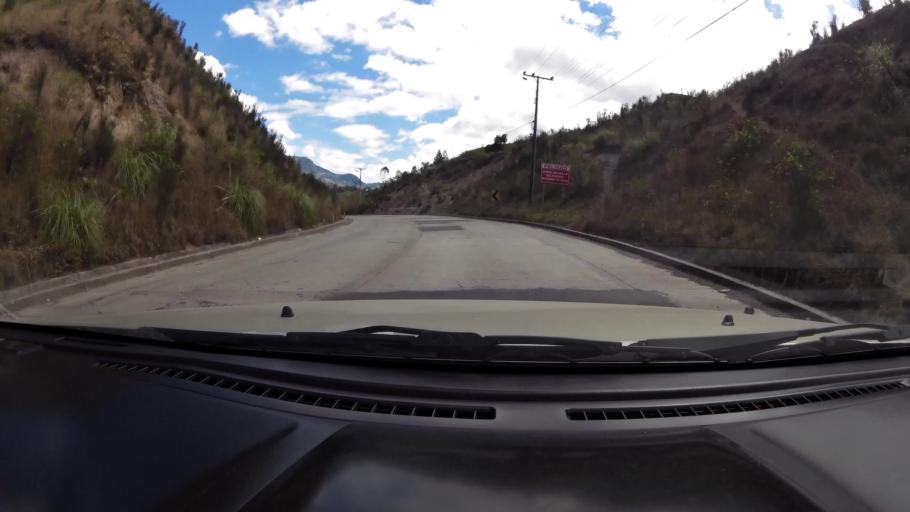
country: EC
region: Azuay
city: Cuenca
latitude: -3.1748
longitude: -79.1622
